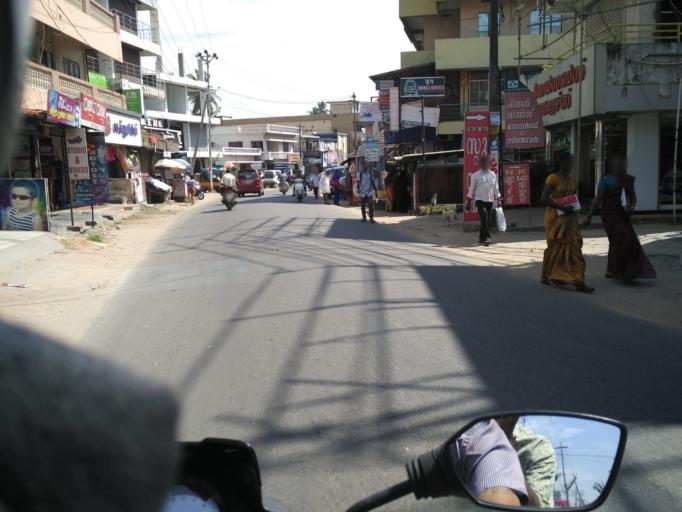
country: IN
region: Kerala
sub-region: Palakkad district
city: Chittur
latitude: 10.5936
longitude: 76.5987
